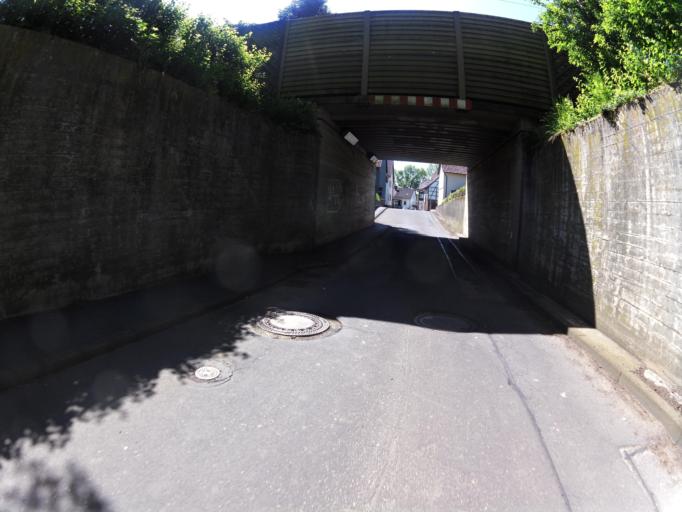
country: DE
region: Thuringia
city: Dankmarshausen
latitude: 50.9515
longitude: 10.0353
